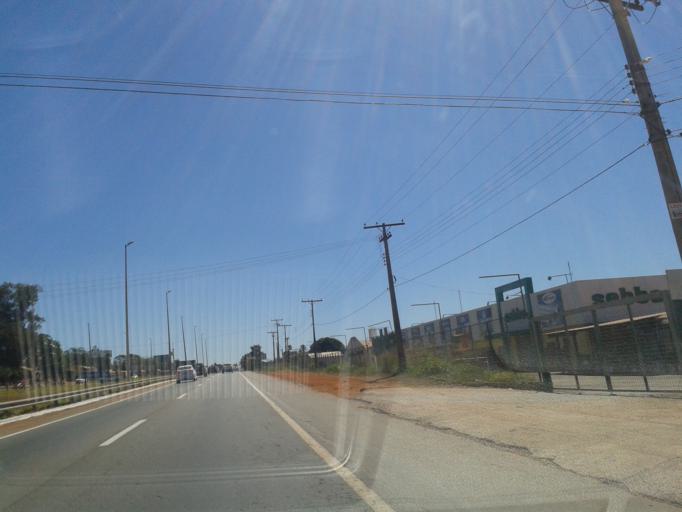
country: BR
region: Goias
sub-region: Goiania
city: Goiania
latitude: -16.6272
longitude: -49.3516
